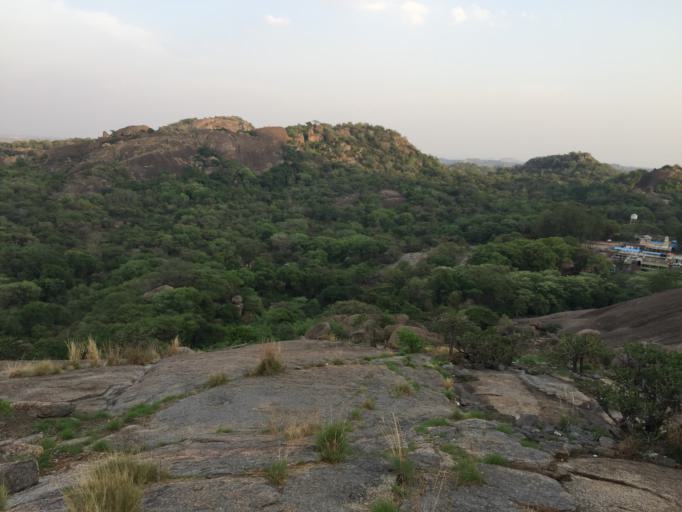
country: IN
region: Karnataka
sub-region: Ramanagara
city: Magadi
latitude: 12.9200
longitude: 77.2986
